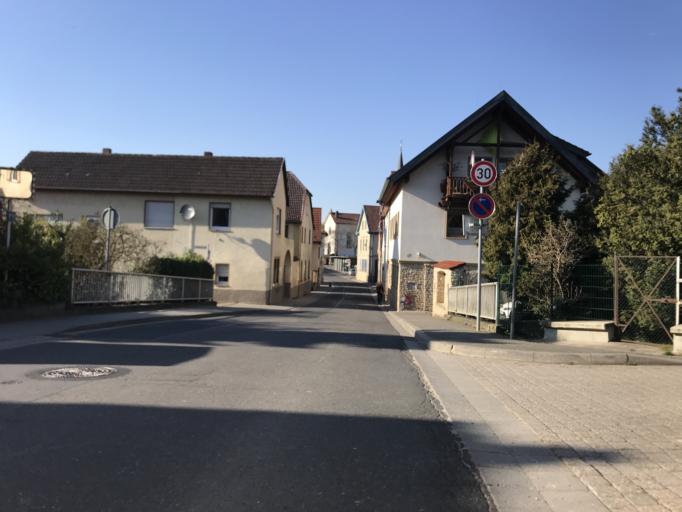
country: DE
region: Rheinland-Pfalz
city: Schwabenheim
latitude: 49.9302
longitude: 8.0981
